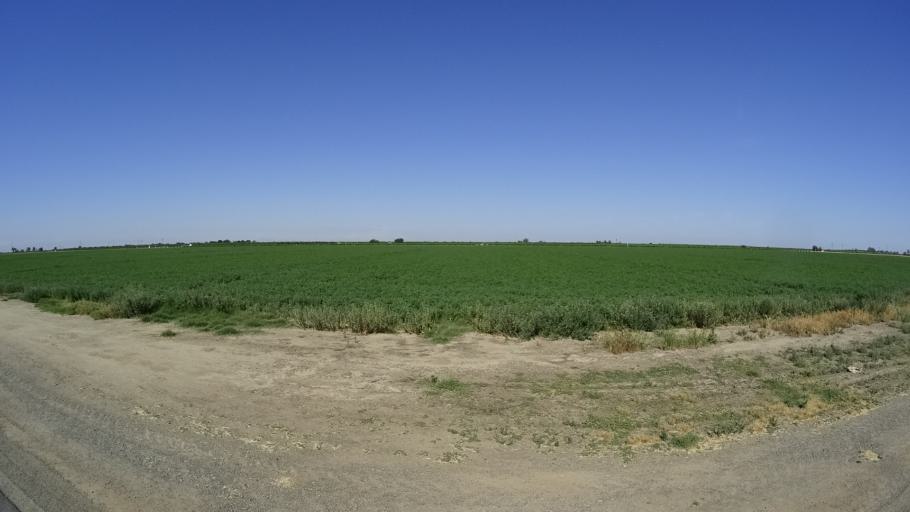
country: US
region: California
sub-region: Kings County
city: Home Garden
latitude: 36.2657
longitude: -119.5474
